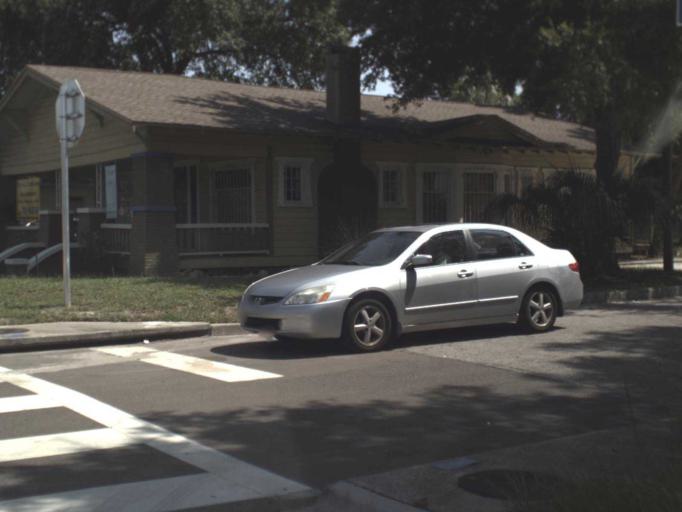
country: US
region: Florida
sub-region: Hillsborough County
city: Egypt Lake-Leto
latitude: 27.9987
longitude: -82.4594
